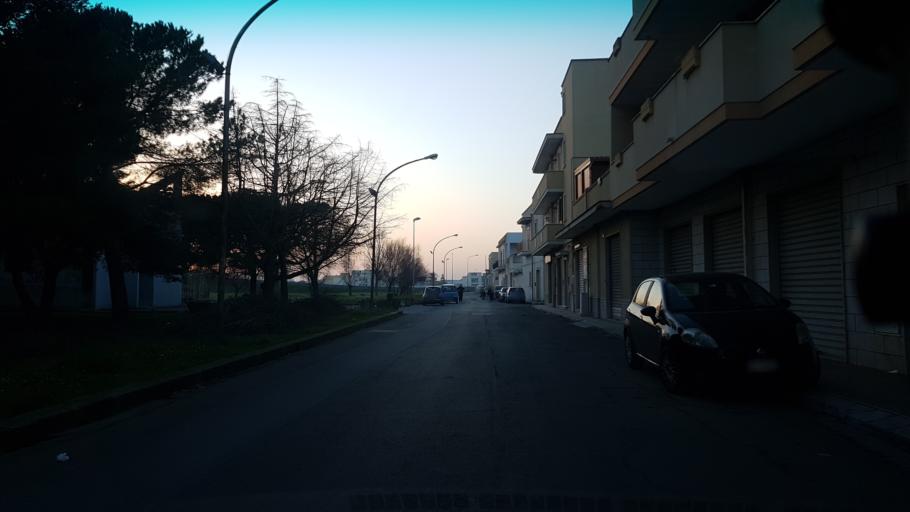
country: IT
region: Apulia
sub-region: Provincia di Brindisi
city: Mesagne
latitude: 40.5613
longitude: 17.7970
